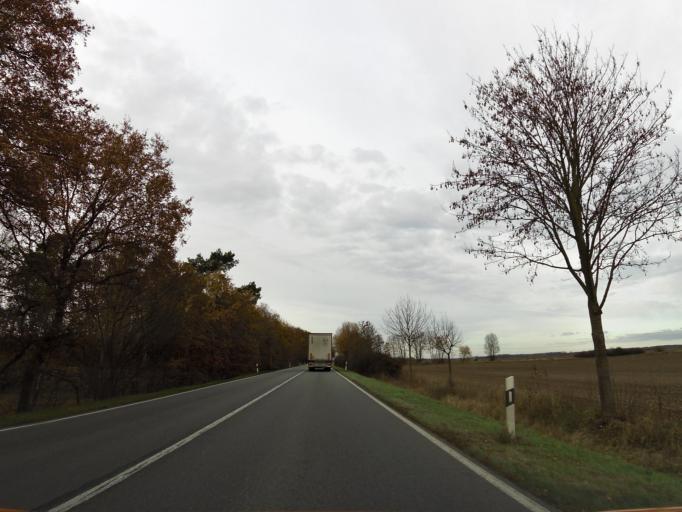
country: DE
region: Saxony-Anhalt
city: Pretzier
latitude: 52.7727
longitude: 11.2357
